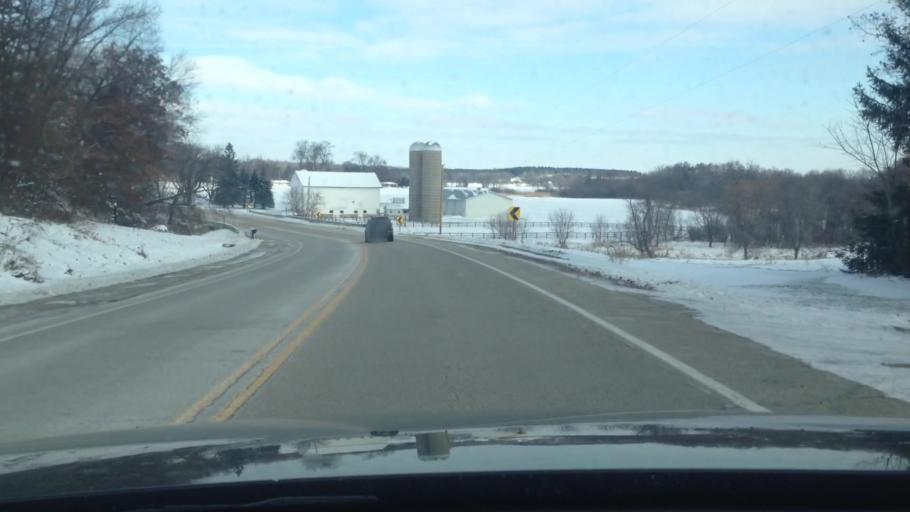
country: US
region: Wisconsin
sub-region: Walworth County
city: Lake Geneva
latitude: 42.6328
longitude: -88.4129
